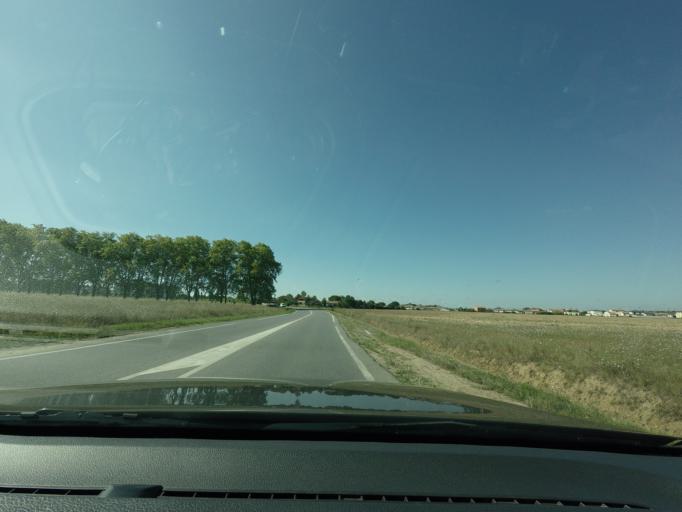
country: FR
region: Midi-Pyrenees
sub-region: Departement de la Haute-Garonne
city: Colomiers
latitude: 43.6288
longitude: 1.3315
